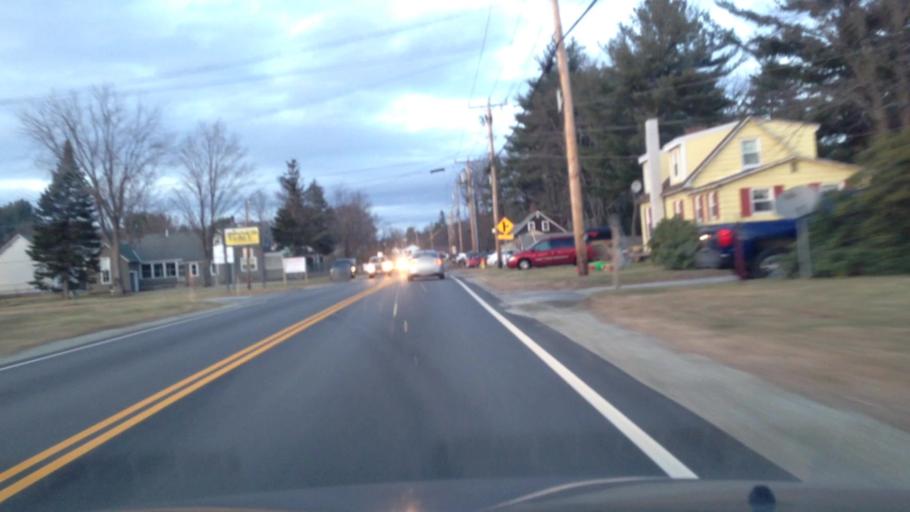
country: US
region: New Hampshire
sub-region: Cheshire County
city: Keene
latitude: 42.9027
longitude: -72.2652
